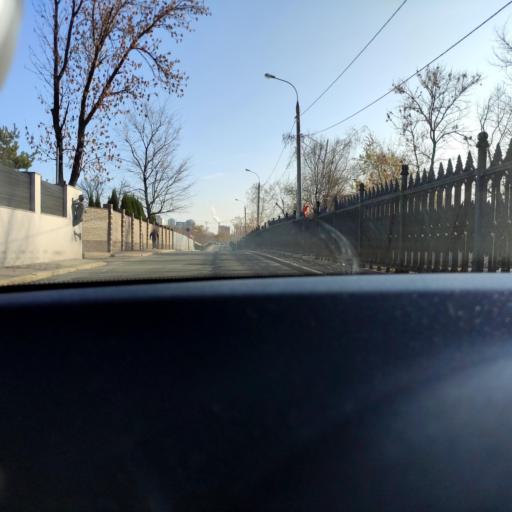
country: RU
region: Samara
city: Samara
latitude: 53.2296
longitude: 50.1713
